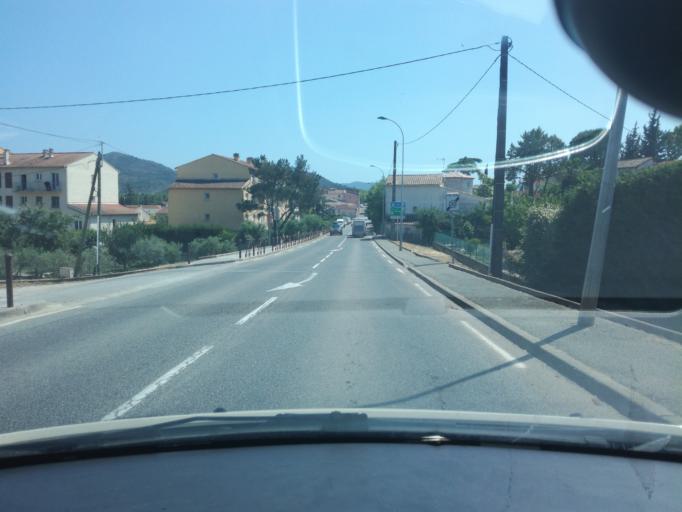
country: FR
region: Provence-Alpes-Cote d'Azur
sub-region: Departement du Var
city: Le Muy
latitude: 43.4772
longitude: 6.5666
